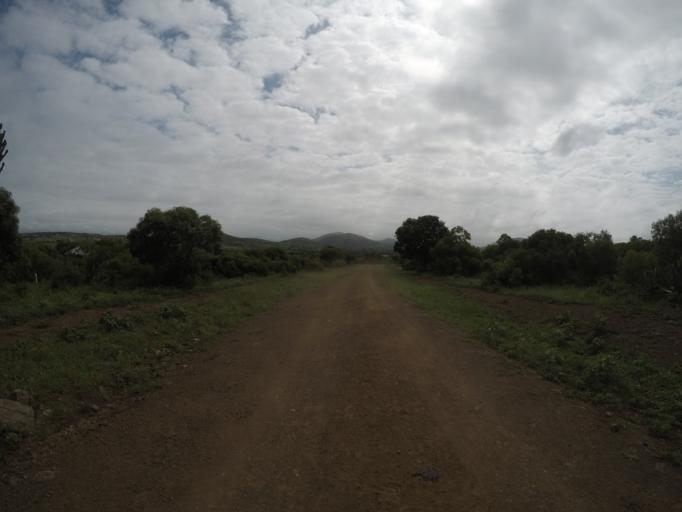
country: ZA
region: KwaZulu-Natal
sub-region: uThungulu District Municipality
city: Empangeni
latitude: -28.6238
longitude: 31.8548
